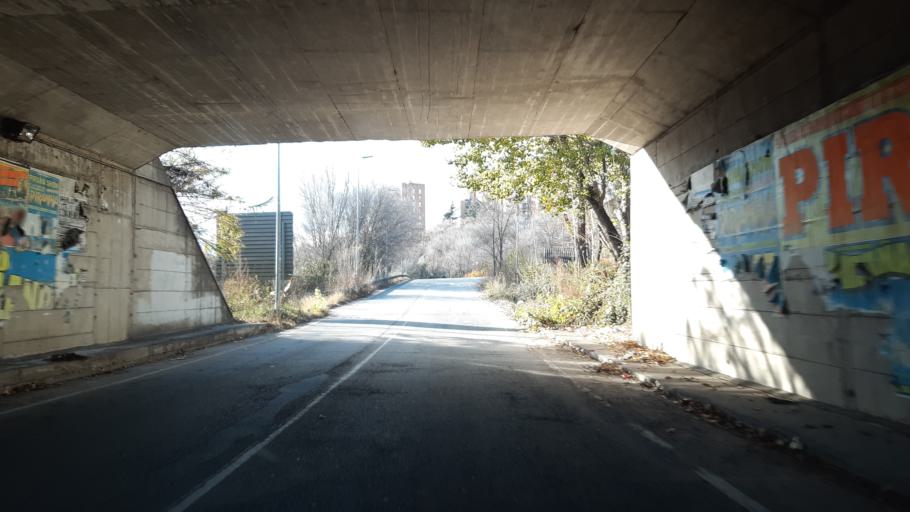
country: ES
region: Catalonia
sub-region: Provincia de Barcelona
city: Vilanova del Cami
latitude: 41.5821
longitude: 1.6354
